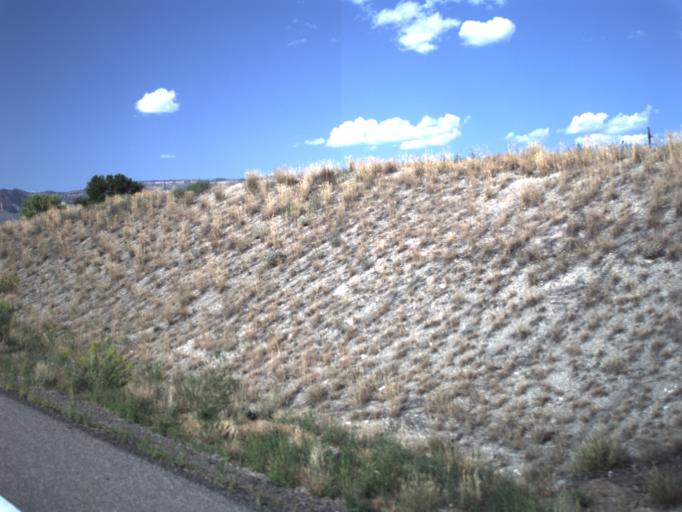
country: US
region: Utah
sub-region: Emery County
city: Ferron
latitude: 39.1017
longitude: -111.1310
